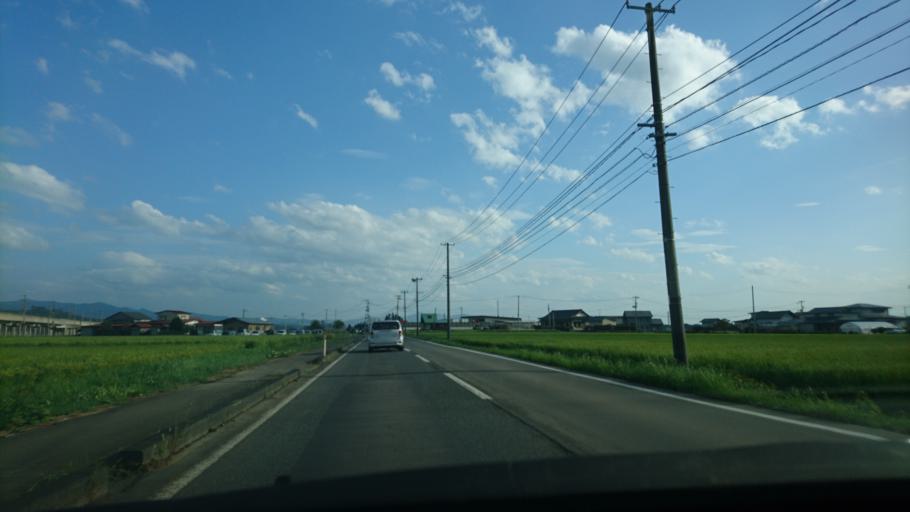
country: JP
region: Iwate
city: Mizusawa
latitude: 39.1712
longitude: 141.1779
